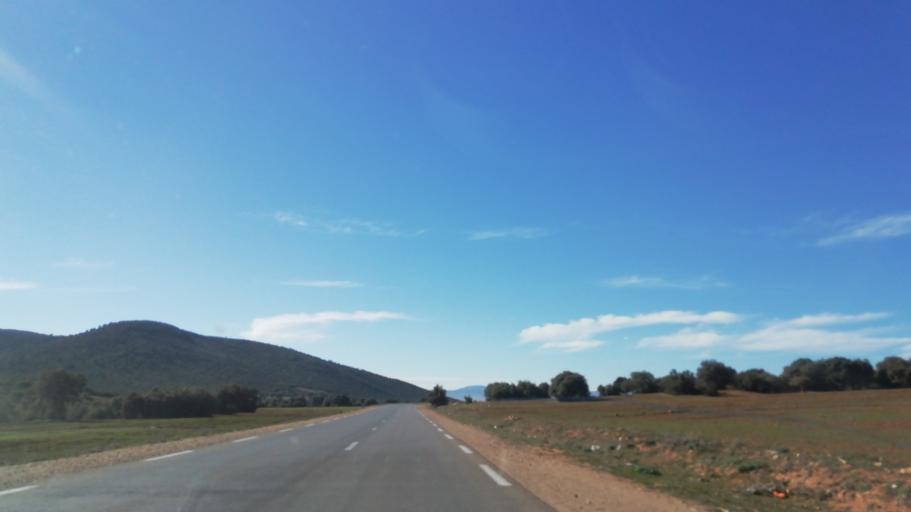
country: DZ
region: Tlemcen
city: Sebdou
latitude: 34.7073
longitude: -1.2155
